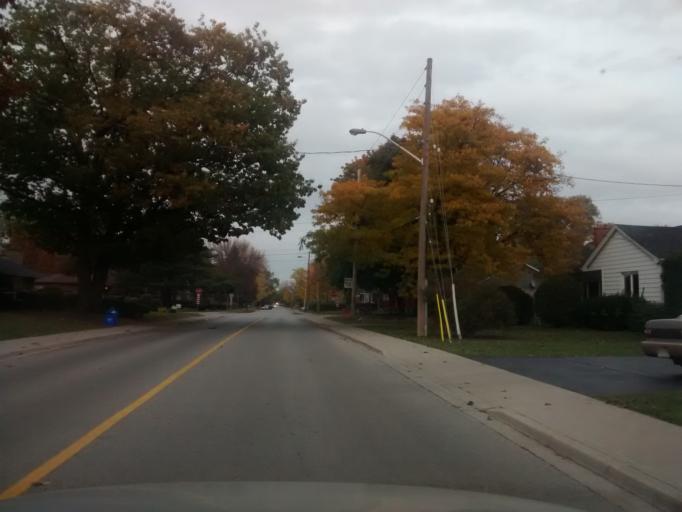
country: CA
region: Ontario
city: Burlington
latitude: 43.3373
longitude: -79.7978
